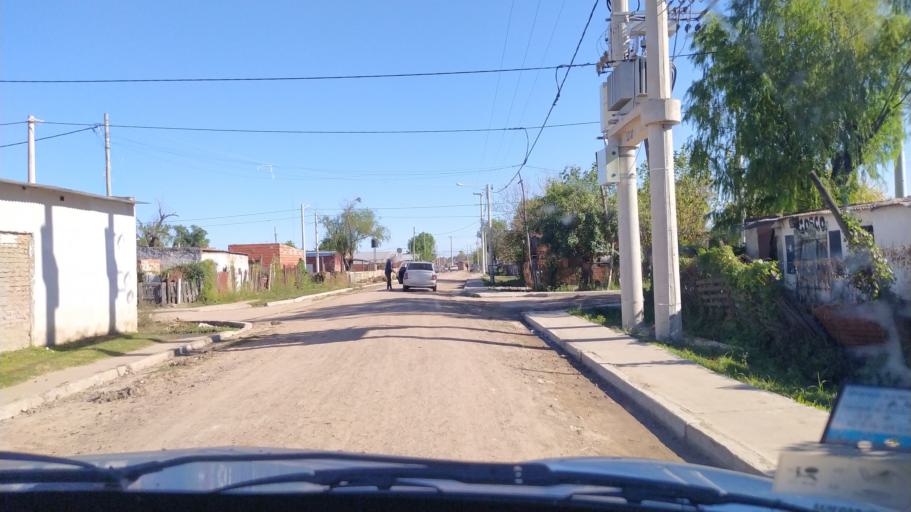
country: AR
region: Corrientes
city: Corrientes
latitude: -27.4960
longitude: -58.8037
